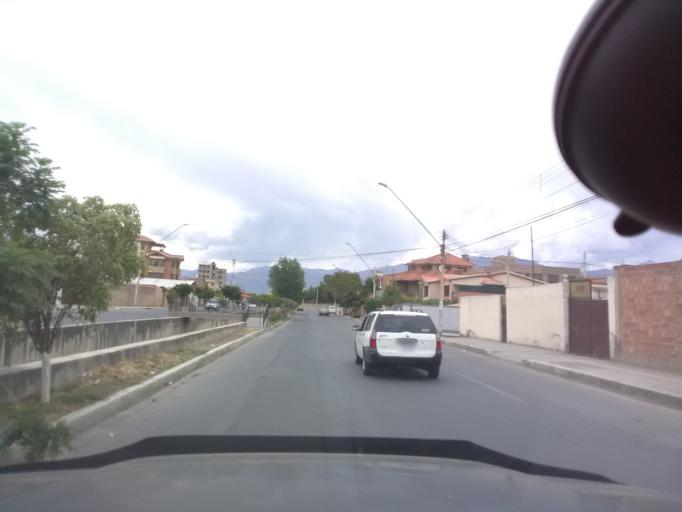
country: BO
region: Cochabamba
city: Cochabamba
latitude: -17.3824
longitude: -66.1907
